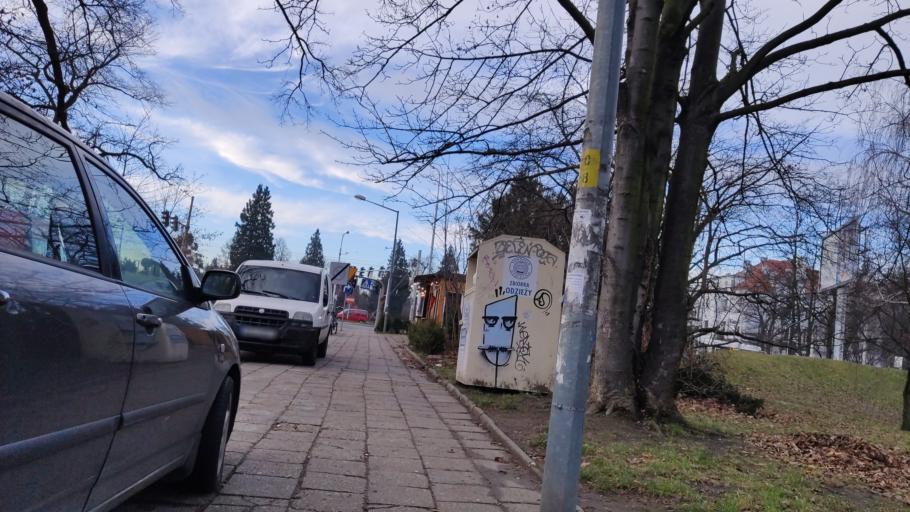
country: PL
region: Lower Silesian Voivodeship
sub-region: Powiat wroclawski
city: Wroclaw
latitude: 51.0795
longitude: 17.0088
